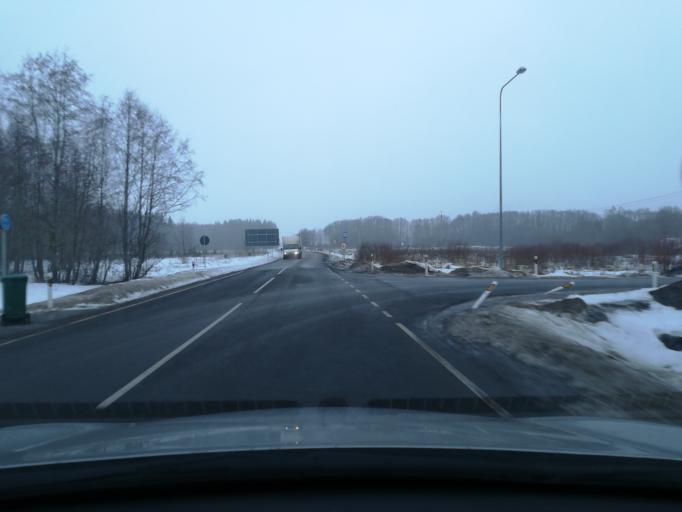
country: EE
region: Harju
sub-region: Rae vald
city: Jueri
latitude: 59.3740
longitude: 24.9046
